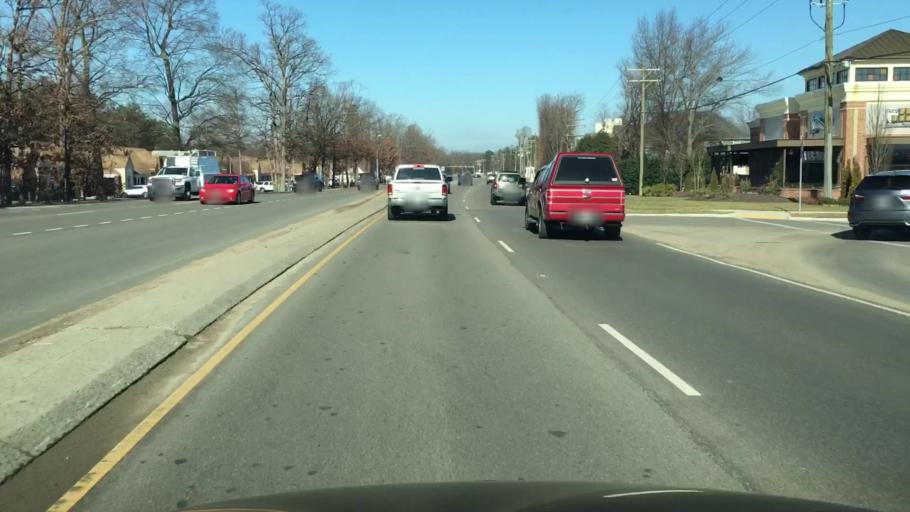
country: US
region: Virginia
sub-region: Chesterfield County
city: Bon Air
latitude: 37.5123
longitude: -77.6145
